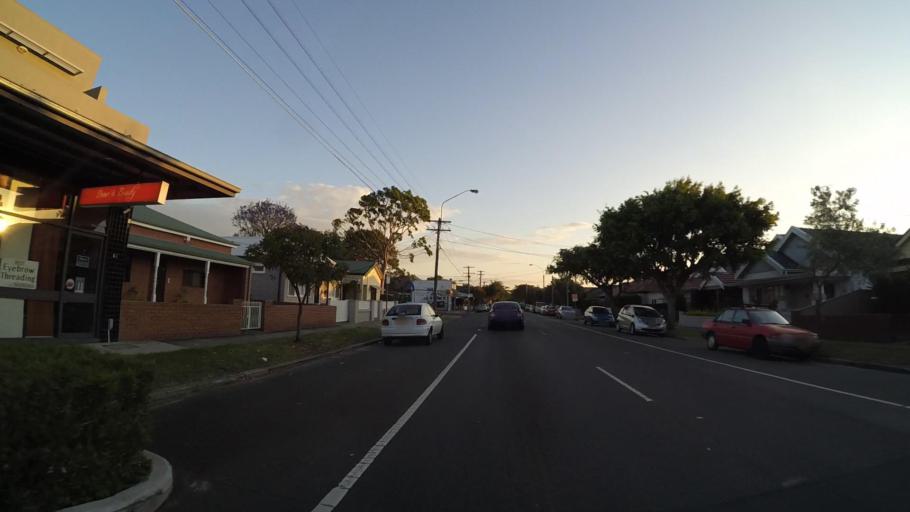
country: AU
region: New South Wales
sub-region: Botany Bay
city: Mascot
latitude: -33.9286
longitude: 151.2058
